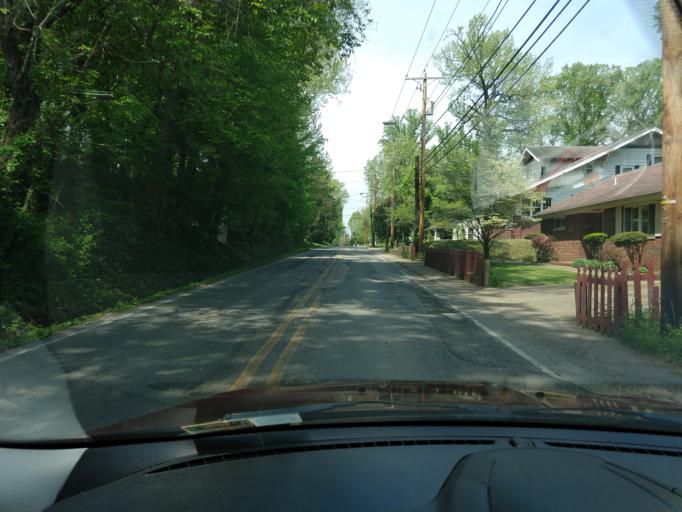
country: US
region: West Virginia
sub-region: Kanawha County
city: Saint Albans
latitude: 38.3760
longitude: -81.7986
